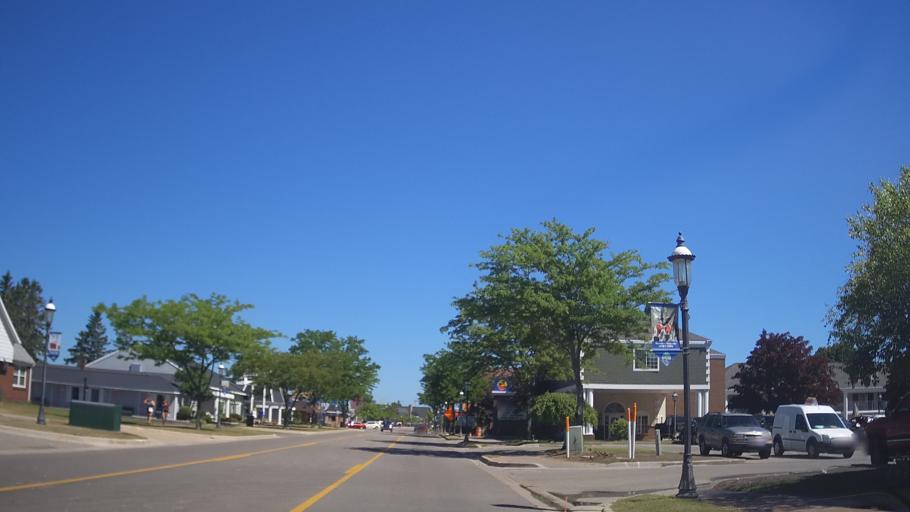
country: US
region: Michigan
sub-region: Mackinac County
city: Saint Ignace
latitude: 45.7750
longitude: -84.7266
